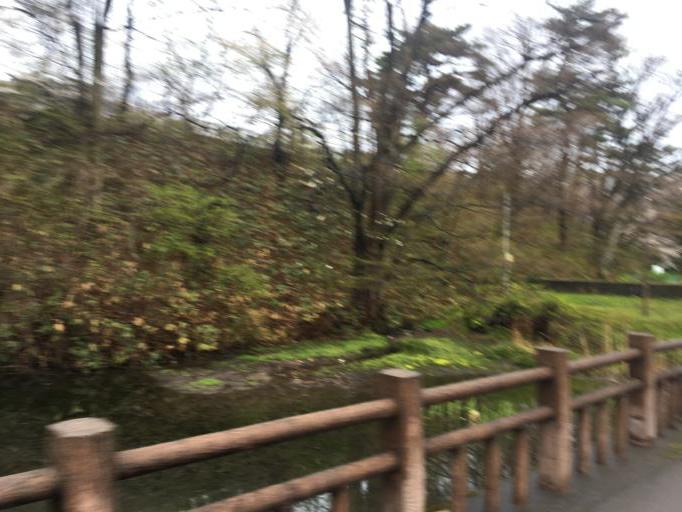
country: JP
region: Akita
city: Akita
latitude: 39.7207
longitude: 140.1257
